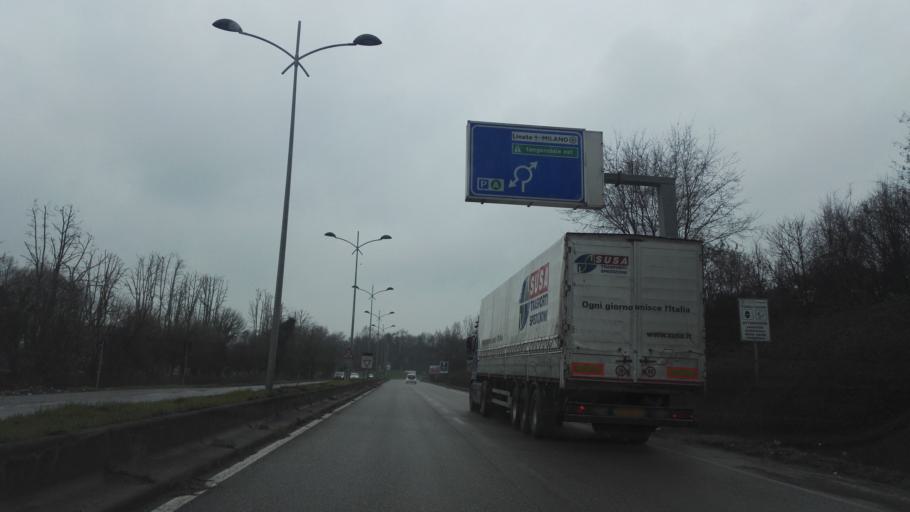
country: IT
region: Lombardy
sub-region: Citta metropolitana di Milano
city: Novegro-Tregarezzo-San Felice
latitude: 45.4681
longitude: 9.2853
